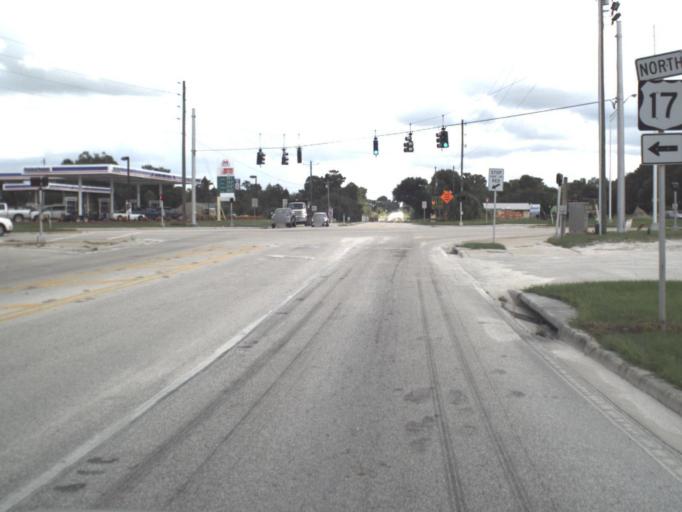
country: US
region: Florida
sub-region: Hardee County
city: Zolfo Springs
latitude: 27.5002
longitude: -81.7986
